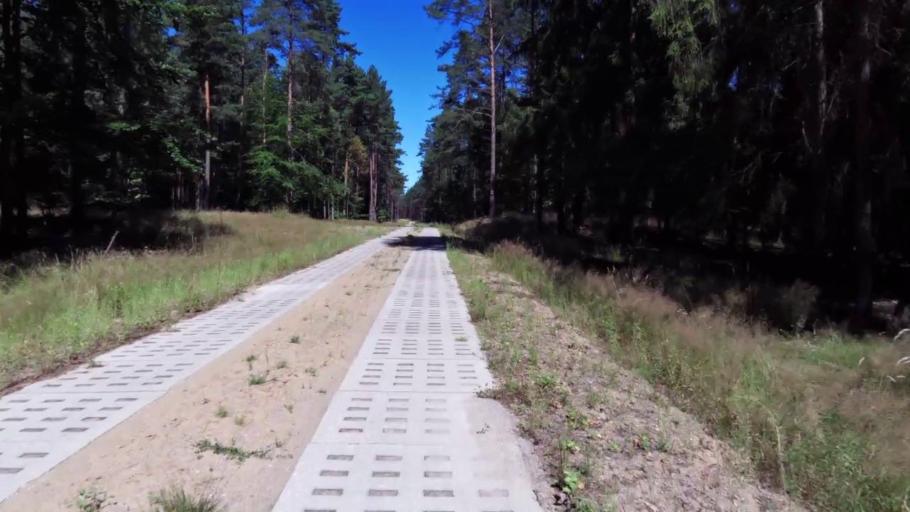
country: PL
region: West Pomeranian Voivodeship
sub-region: Powiat szczecinecki
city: Szczecinek
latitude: 53.6089
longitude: 16.6643
